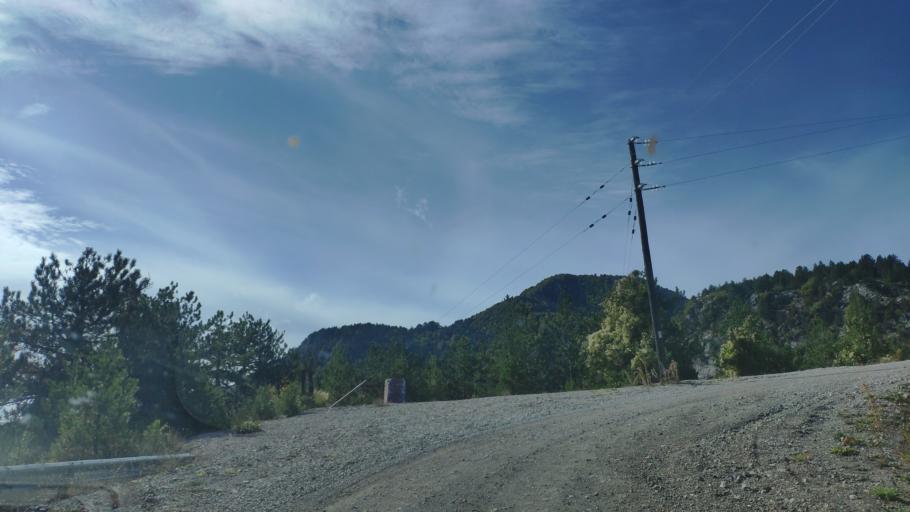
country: AL
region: Korce
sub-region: Rrethi i Devollit
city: Miras
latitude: 40.4118
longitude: 20.8680
